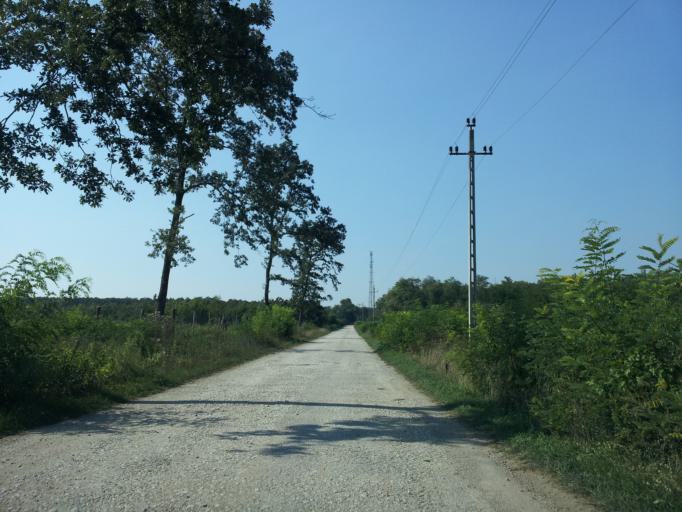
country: HU
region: Fejer
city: Polgardi
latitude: 47.0267
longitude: 18.2782
